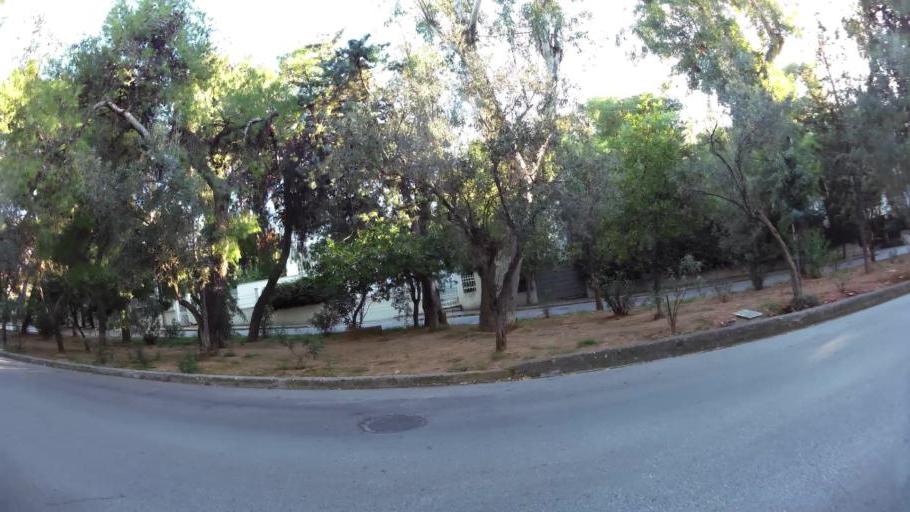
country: GR
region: Attica
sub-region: Nomarchia Athinas
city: Nea Erythraia
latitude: 38.0841
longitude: 23.8295
